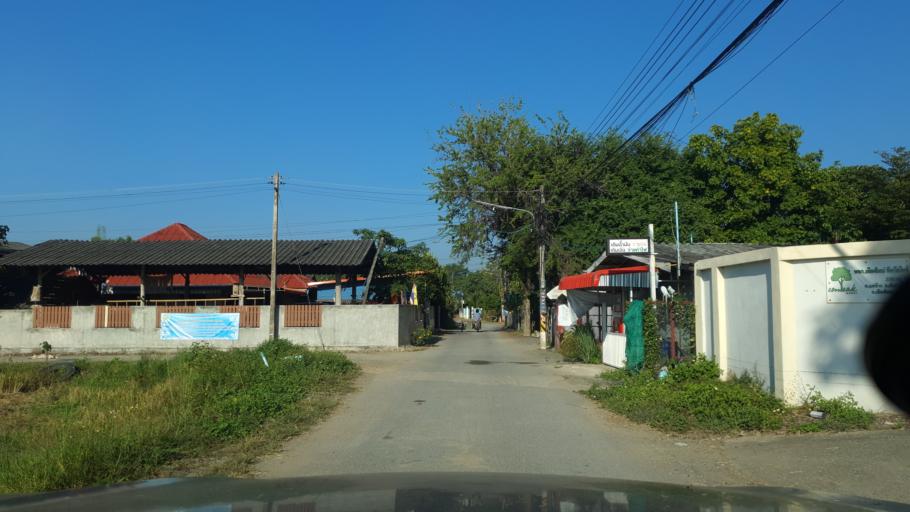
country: TH
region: Chiang Mai
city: San Kamphaeng
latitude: 18.7149
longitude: 99.1473
